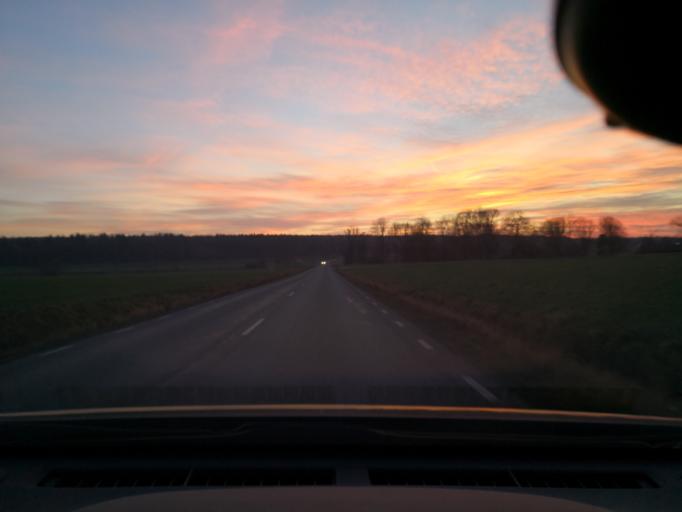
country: SE
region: OErebro
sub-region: Lindesbergs Kommun
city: Fellingsbro
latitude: 59.4275
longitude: 15.5736
